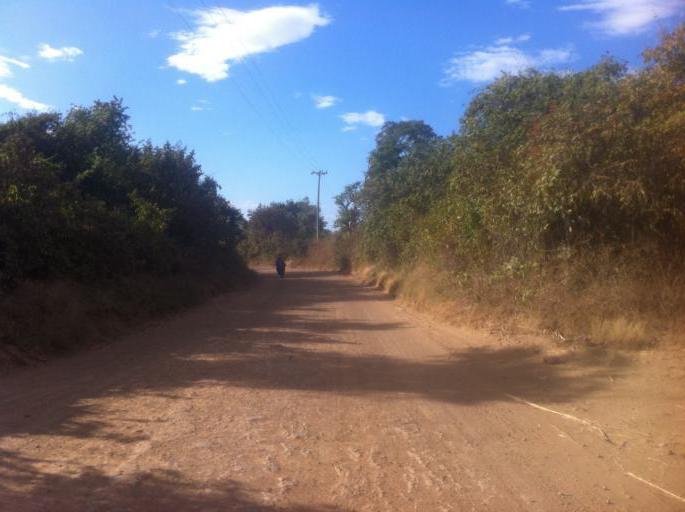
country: NI
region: Managua
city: Masachapa
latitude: 11.8187
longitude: -86.4964
